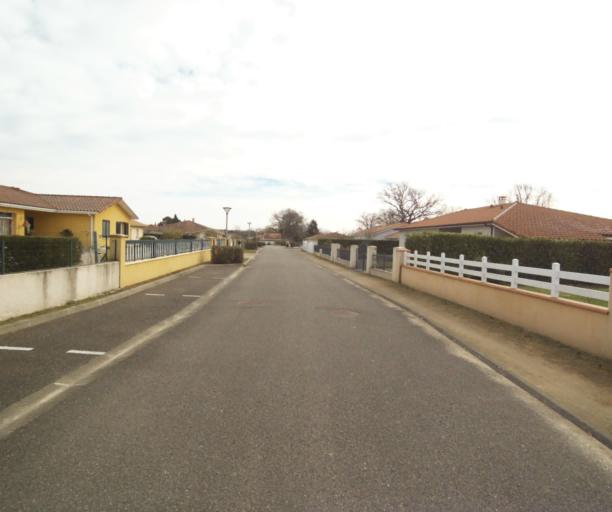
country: FR
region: Aquitaine
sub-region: Departement des Landes
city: Gabarret
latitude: 43.9848
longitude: 0.0039
